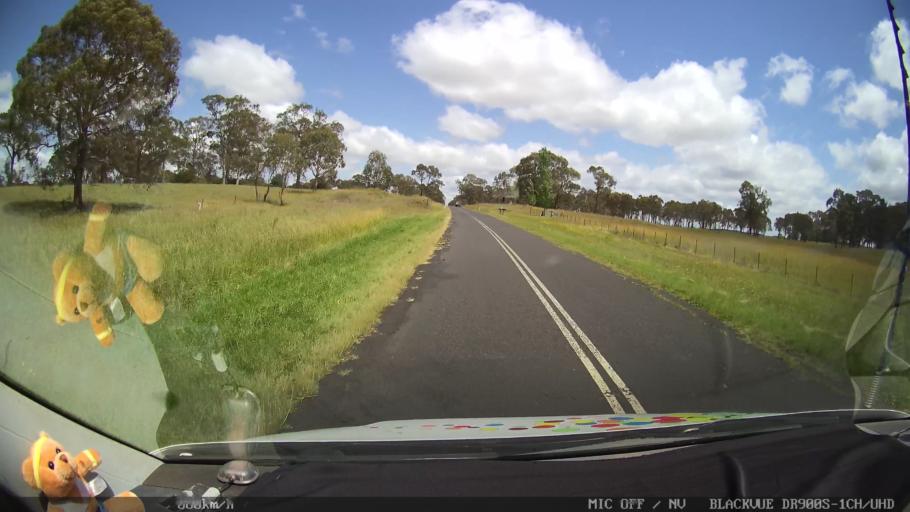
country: AU
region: New South Wales
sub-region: Glen Innes Severn
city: Glen Innes
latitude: -29.6381
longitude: 151.6857
